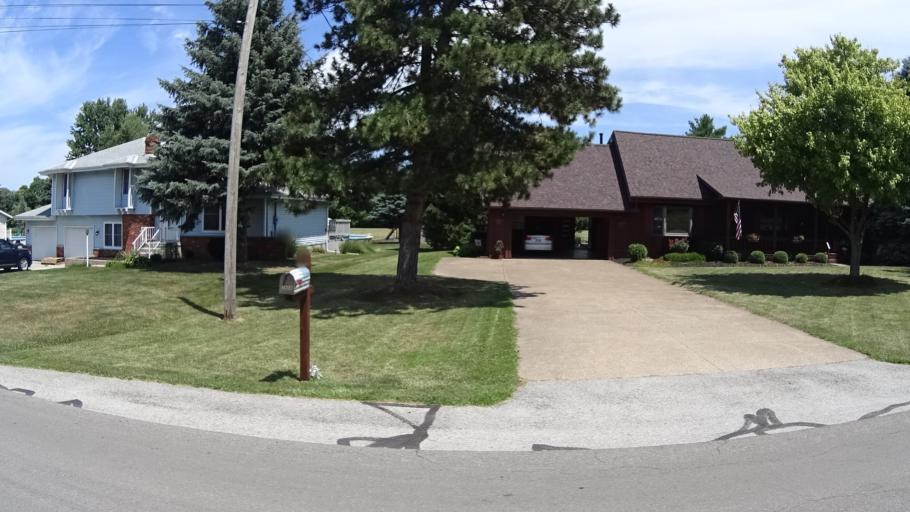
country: US
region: Ohio
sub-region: Erie County
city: Sandusky
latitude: 41.4000
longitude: -82.7881
